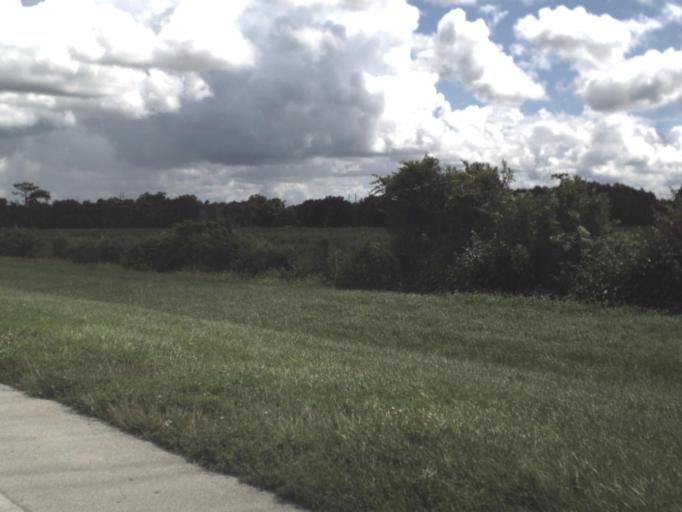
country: US
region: Florida
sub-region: DeSoto County
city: Southeast Arcadia
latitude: 27.2088
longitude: -81.8155
